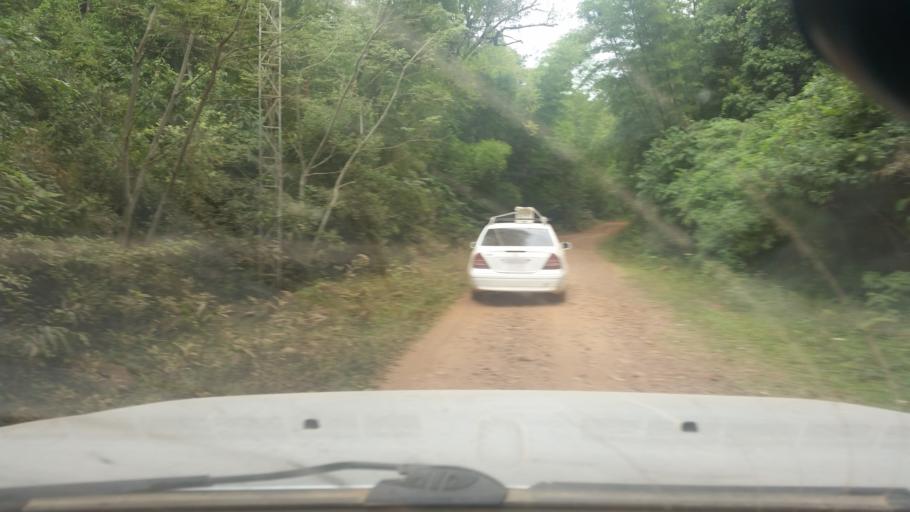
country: PY
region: Guaira
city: Independencia
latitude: -25.8156
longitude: -56.2746
